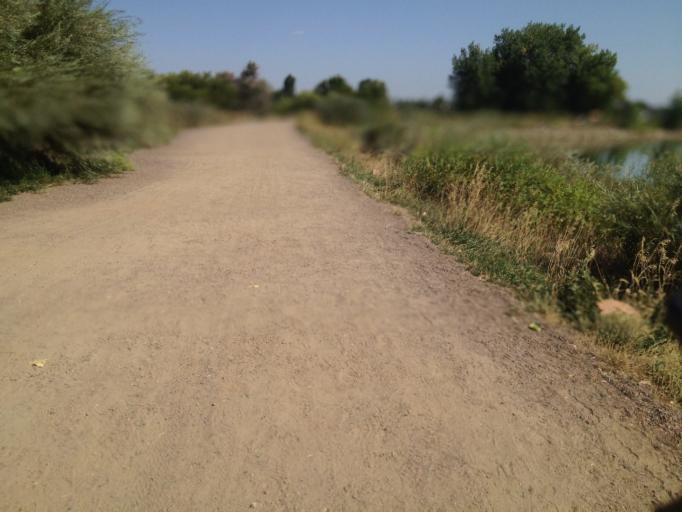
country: US
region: Colorado
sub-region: Boulder County
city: Lafayette
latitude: 39.9970
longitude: -105.1102
